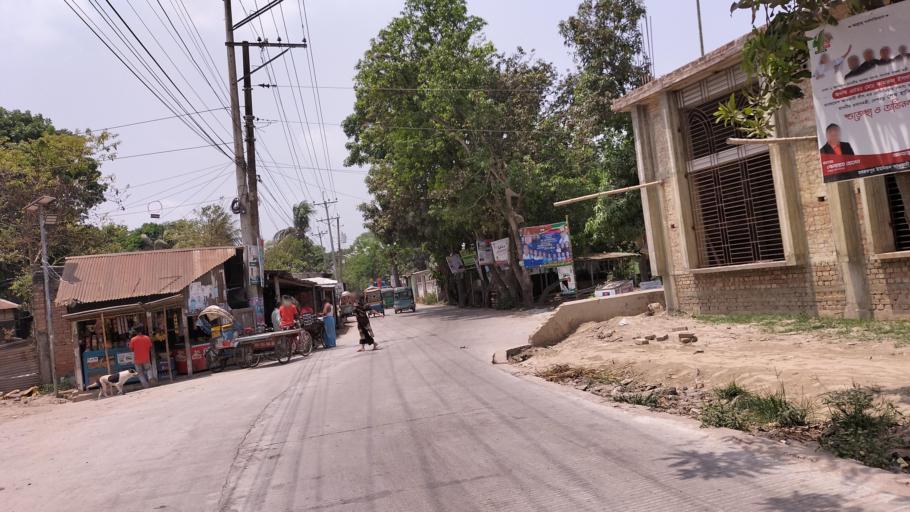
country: BD
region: Dhaka
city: Azimpur
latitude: 23.7335
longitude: 90.2689
